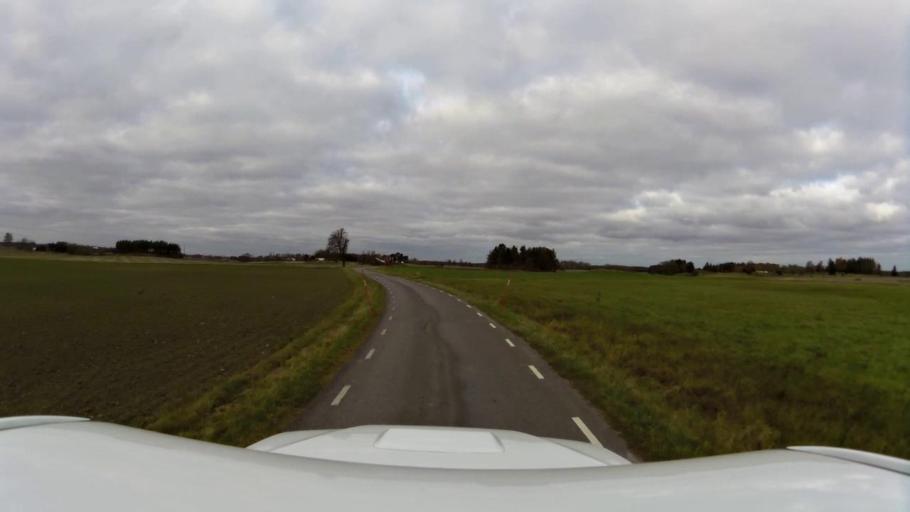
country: SE
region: OEstergoetland
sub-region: Linkopings Kommun
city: Linghem
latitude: 58.3951
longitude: 15.7949
